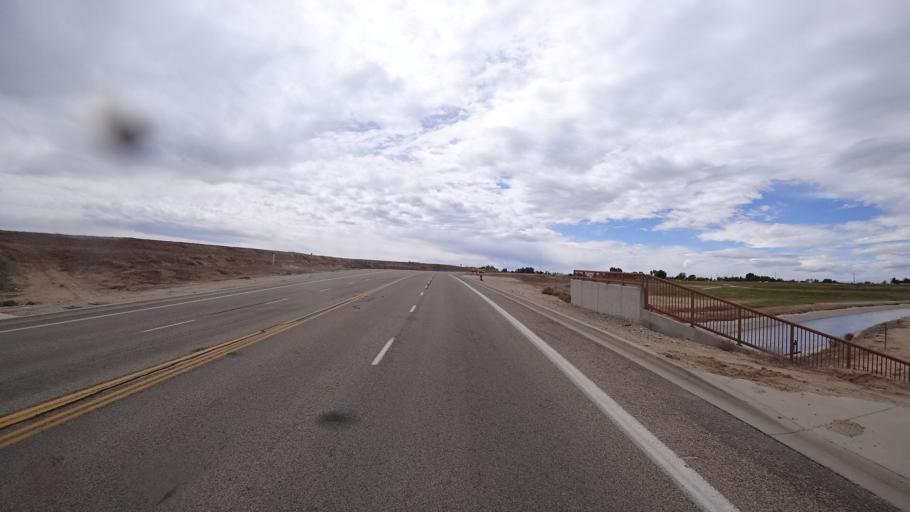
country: US
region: Idaho
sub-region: Ada County
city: Meridian
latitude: 43.5881
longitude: -116.4281
